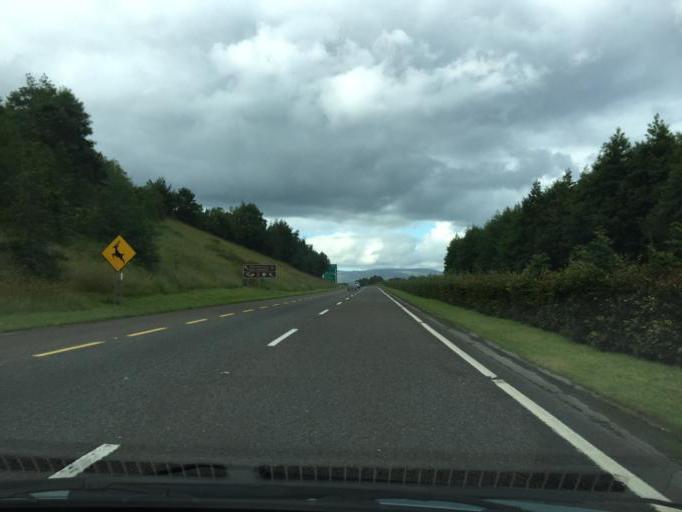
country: IE
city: Ballisodare
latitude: 54.2108
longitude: -8.5021
